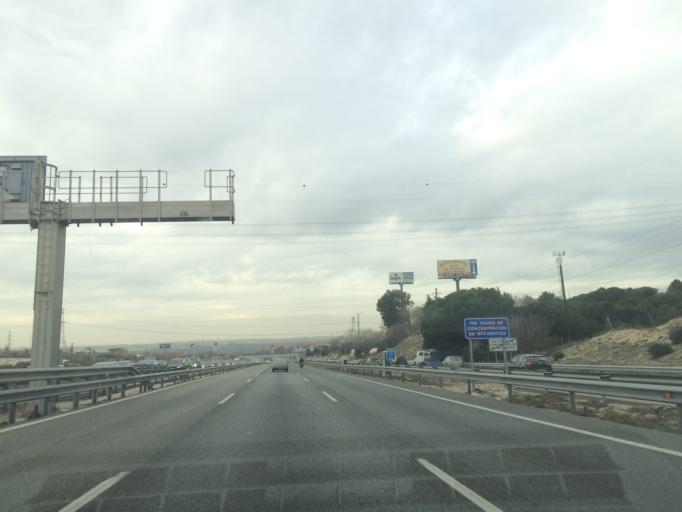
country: ES
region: Madrid
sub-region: Provincia de Madrid
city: Arroyomolinos
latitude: 40.3039
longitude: -3.9135
